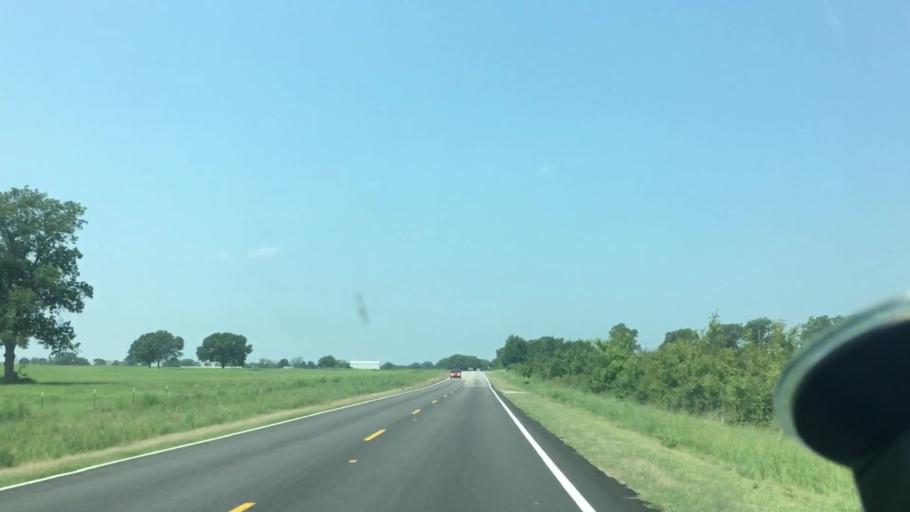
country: US
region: Oklahoma
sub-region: Atoka County
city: Atoka
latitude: 34.2790
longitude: -95.9407
